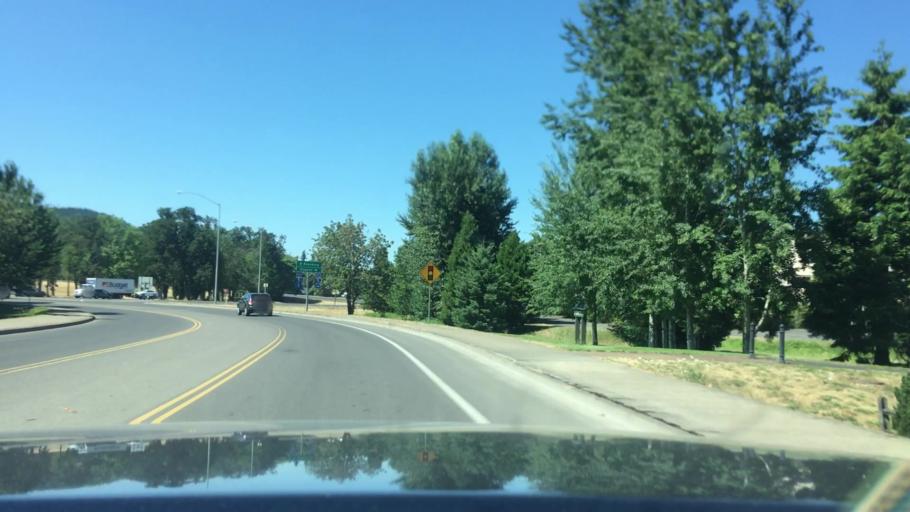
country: US
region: Oregon
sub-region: Lane County
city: Cottage Grove
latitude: 43.8033
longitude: -123.0406
